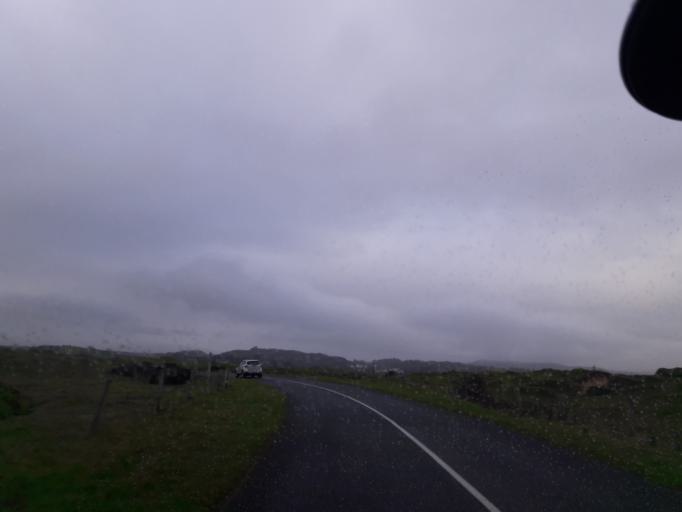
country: IE
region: Ulster
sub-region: County Donegal
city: Ramelton
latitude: 55.1891
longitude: -7.6120
